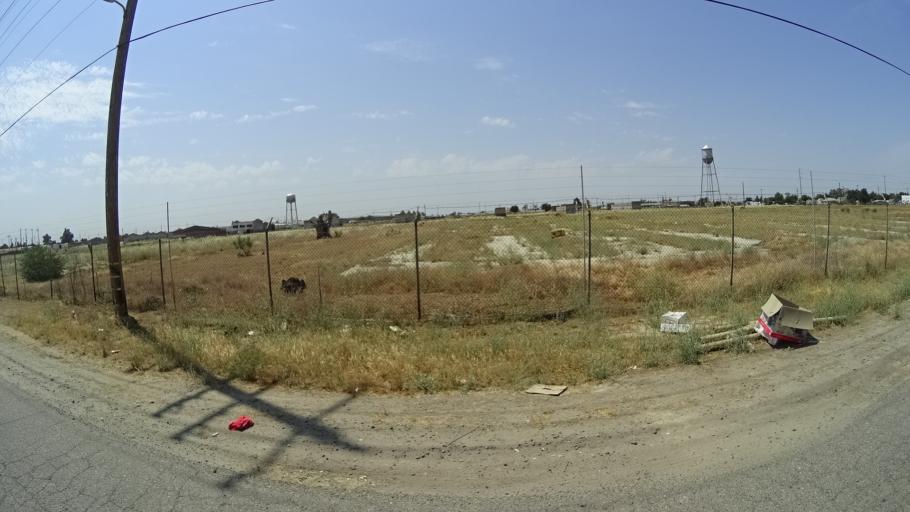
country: US
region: California
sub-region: Fresno County
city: Fresno
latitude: 36.7197
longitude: -119.7700
